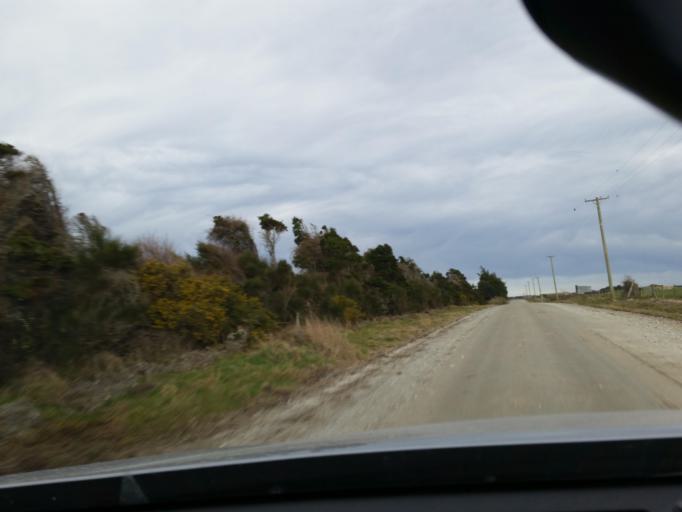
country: NZ
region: Southland
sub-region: Invercargill City
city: Invercargill
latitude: -46.4273
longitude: 168.5062
